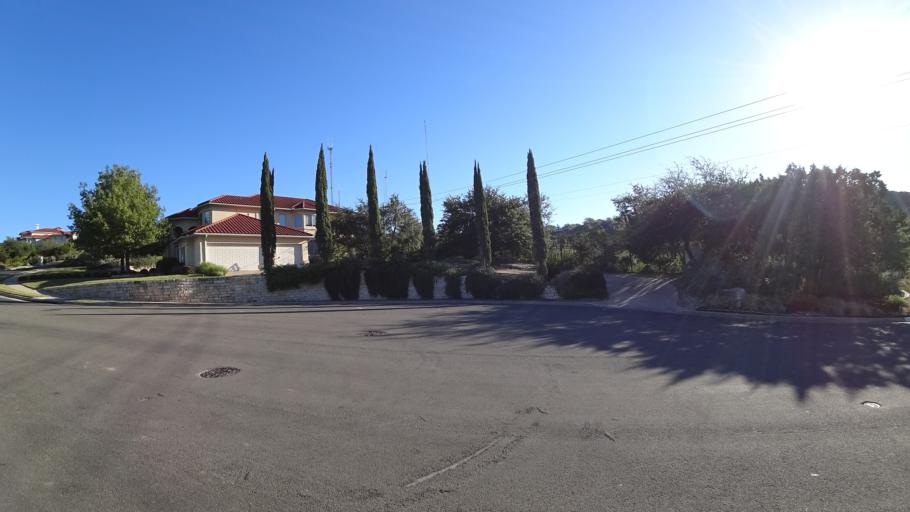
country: US
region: Texas
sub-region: Travis County
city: West Lake Hills
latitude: 30.3151
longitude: -97.8098
